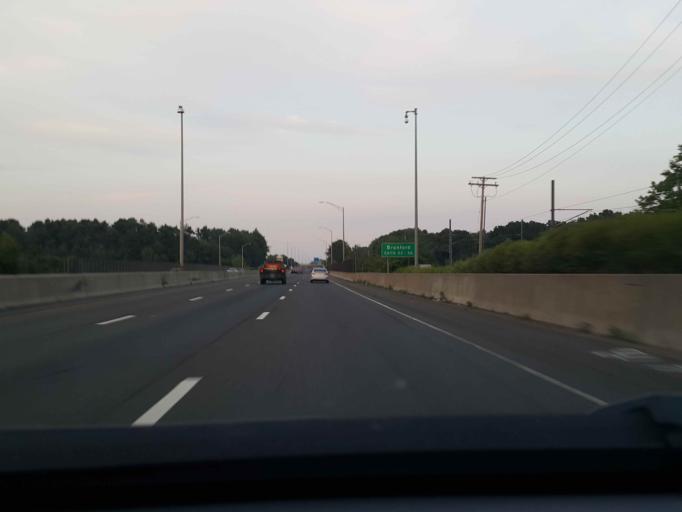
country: US
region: Connecticut
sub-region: New Haven County
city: East Haven
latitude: 41.2818
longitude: -72.8627
